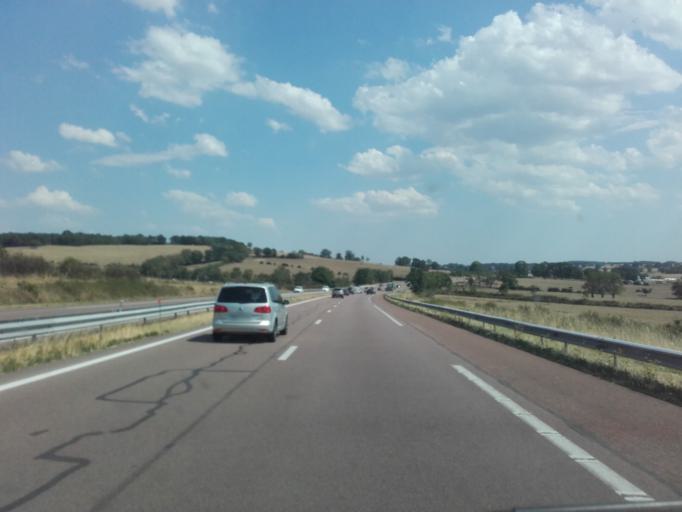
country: FR
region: Bourgogne
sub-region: Departement de l'Yonne
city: Avallon
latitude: 47.5507
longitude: 3.9602
